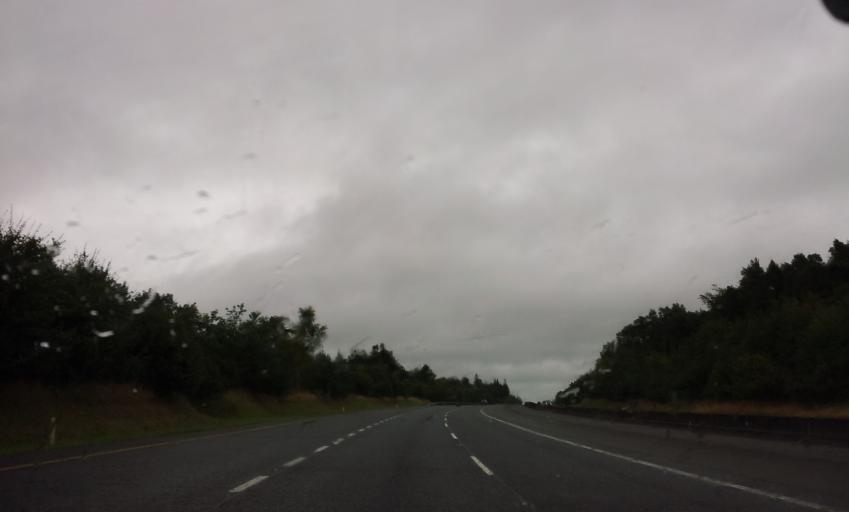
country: IE
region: Munster
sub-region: County Cork
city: Fermoy
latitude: 52.1193
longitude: -8.2707
